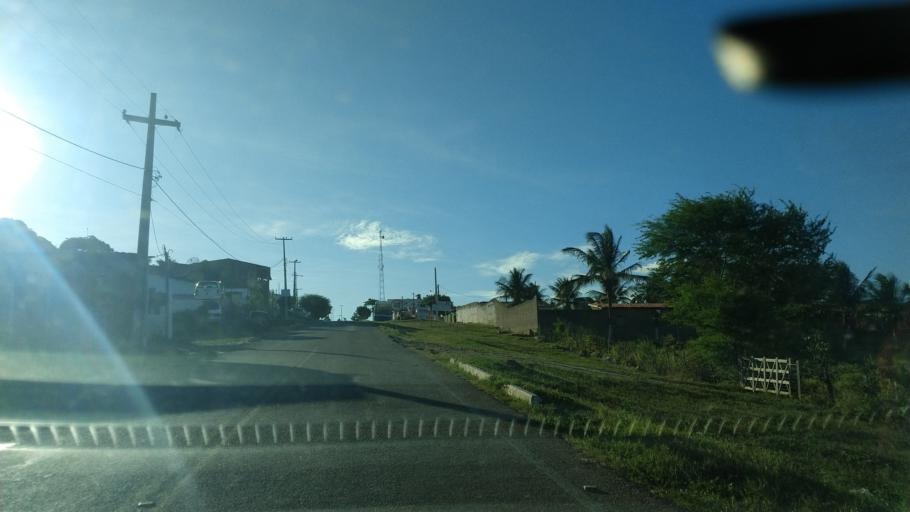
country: BR
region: Rio Grande do Norte
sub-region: Tangara
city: Tangara
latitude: -6.2028
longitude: -35.7986
